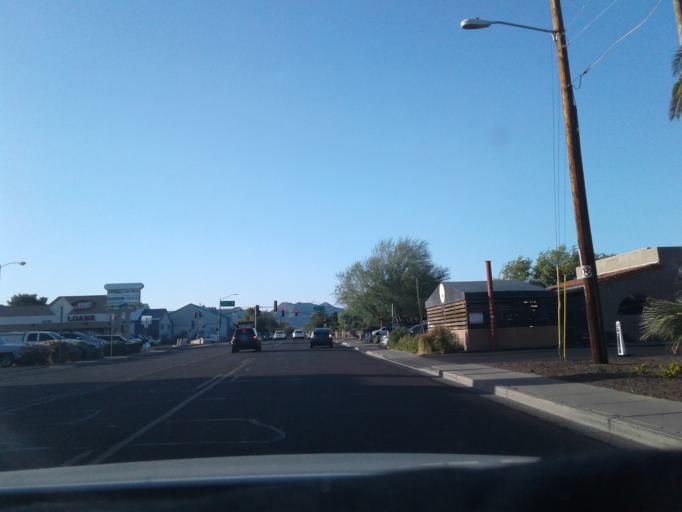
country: US
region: Arizona
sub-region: Maricopa County
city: Paradise Valley
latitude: 33.4939
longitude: -111.9954
